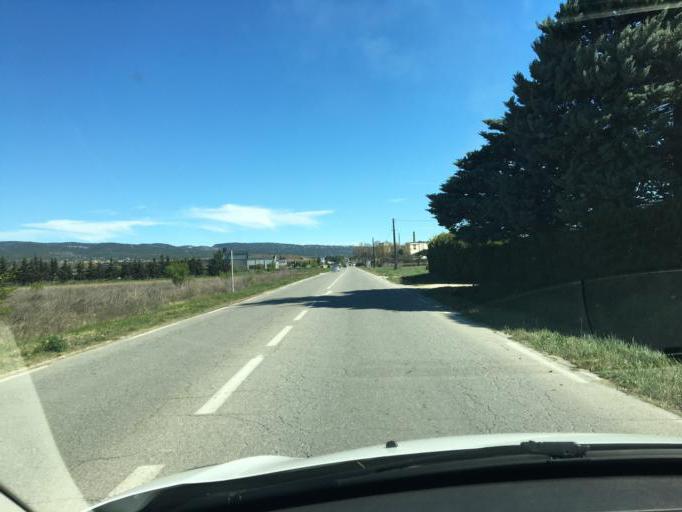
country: FR
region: Provence-Alpes-Cote d'Azur
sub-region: Departement du Vaucluse
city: Maubec
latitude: 43.8626
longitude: 5.1357
